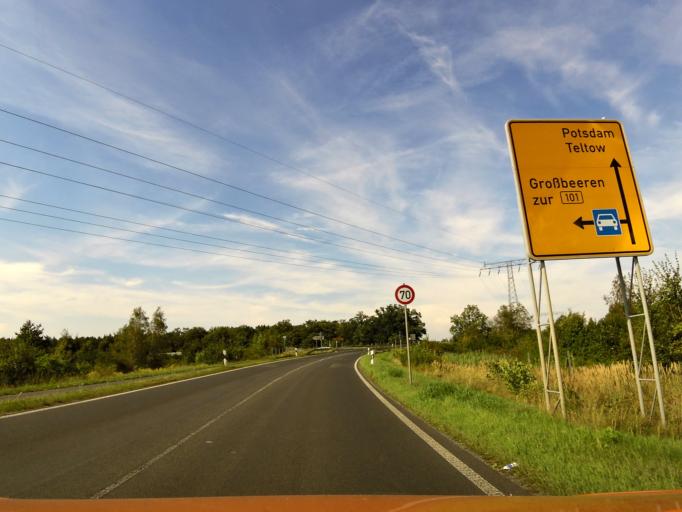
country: DE
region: Brandenburg
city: Grossbeeren
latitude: 52.3565
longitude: 13.2696
